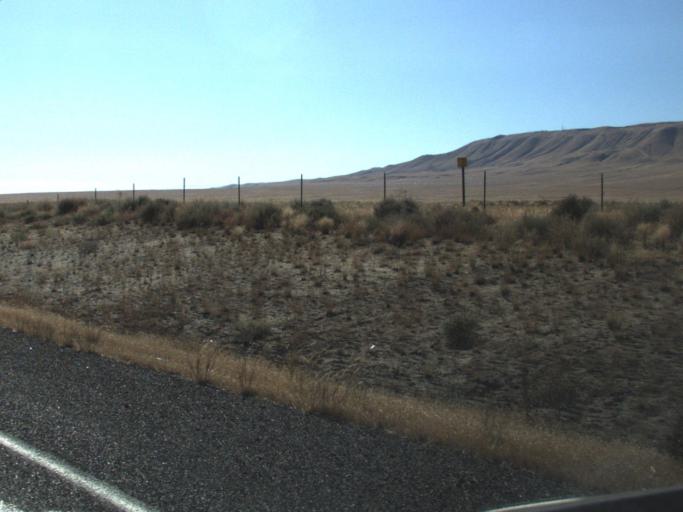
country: US
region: Washington
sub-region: Benton County
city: Benton City
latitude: 46.5002
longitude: -119.6121
